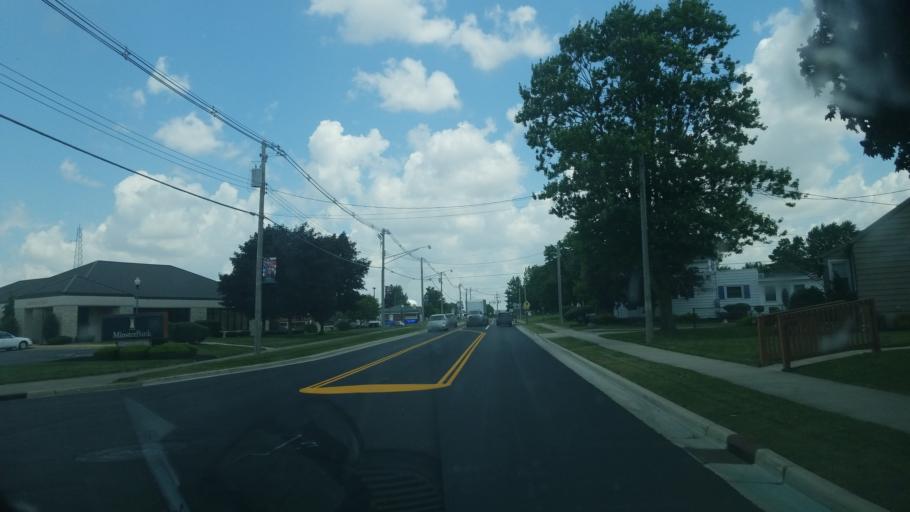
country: US
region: Ohio
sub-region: Auglaize County
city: Wapakoneta
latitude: 40.5770
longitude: -84.2014
